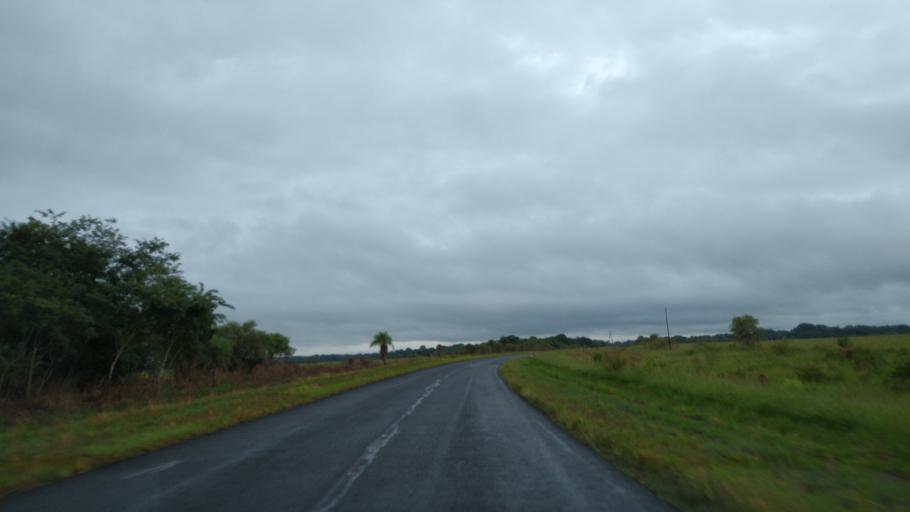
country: AR
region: Corrientes
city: Loreto
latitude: -27.6888
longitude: -57.2158
